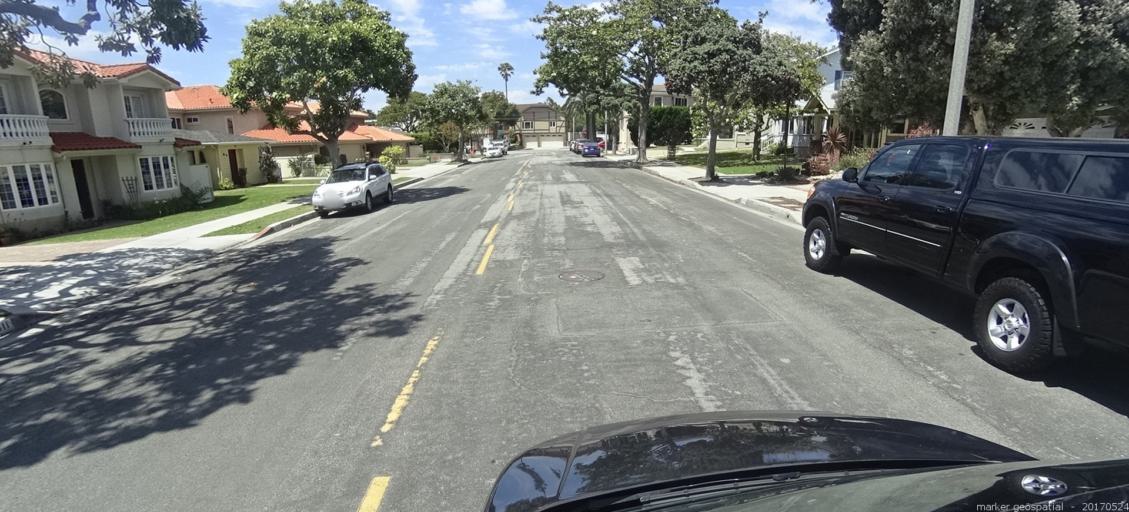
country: US
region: California
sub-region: Los Angeles County
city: Redondo Beach
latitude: 33.8320
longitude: -118.3861
